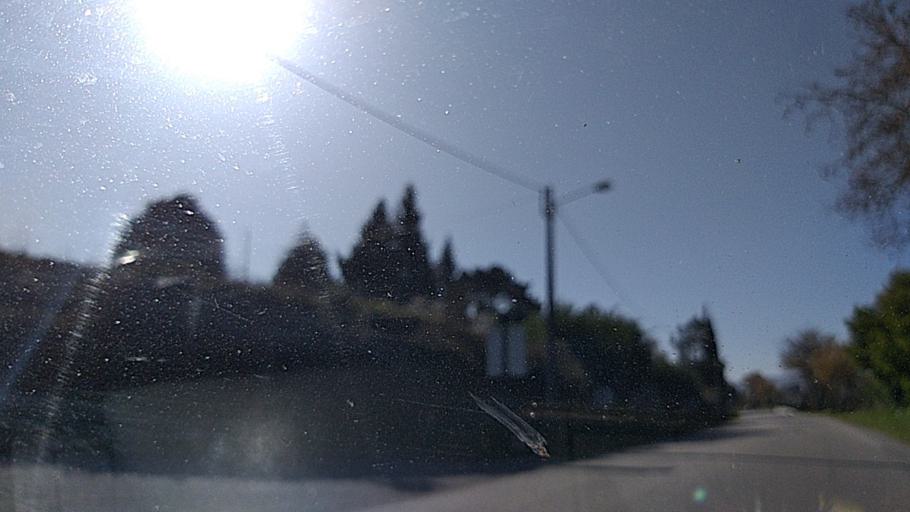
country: PT
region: Guarda
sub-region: Celorico da Beira
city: Celorico da Beira
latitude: 40.6621
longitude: -7.3819
